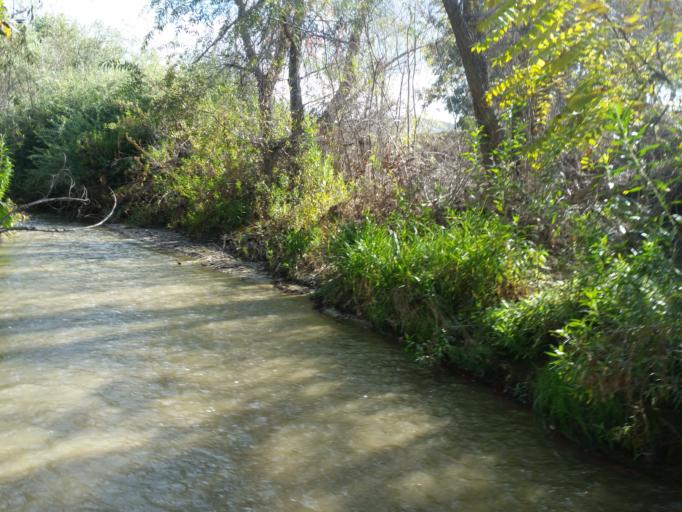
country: US
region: California
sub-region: San Bernardino County
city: Redlands
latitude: 34.0166
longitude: -117.1828
